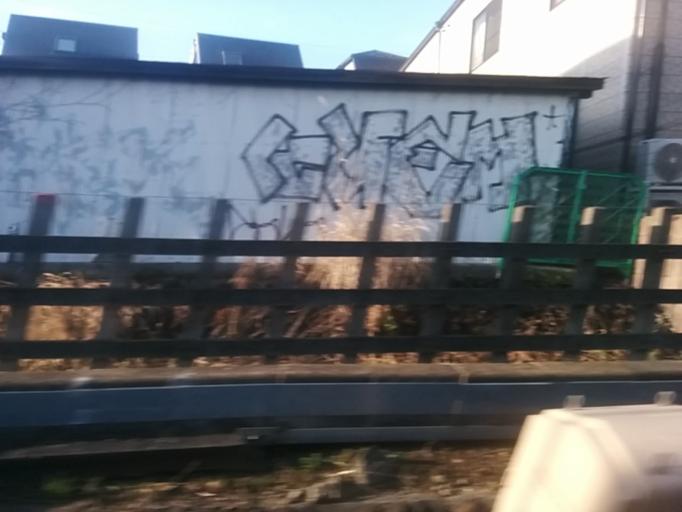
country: JP
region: Saitama
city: Wako
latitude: 35.7744
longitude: 139.6377
